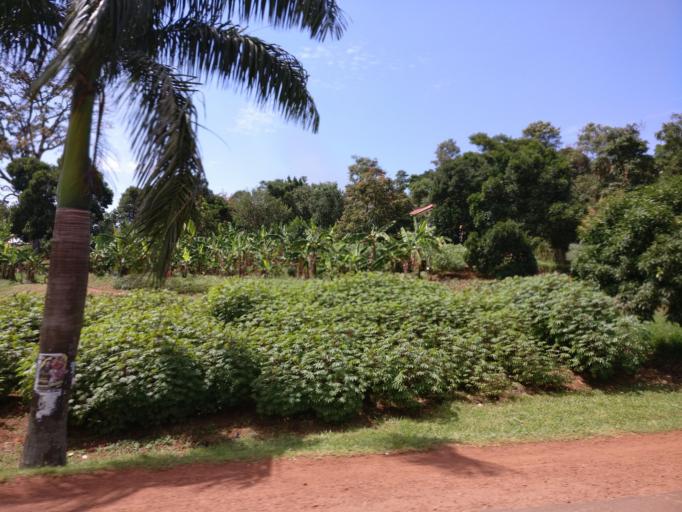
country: UG
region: Central Region
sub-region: Wakiso District
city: Kajansi
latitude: 0.1587
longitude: 32.5457
